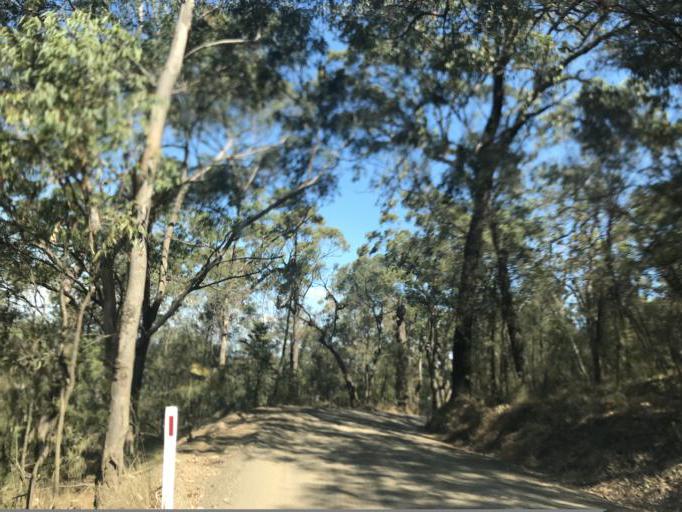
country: AU
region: New South Wales
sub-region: Hawkesbury
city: Pitt Town
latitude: -33.4095
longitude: 150.9235
